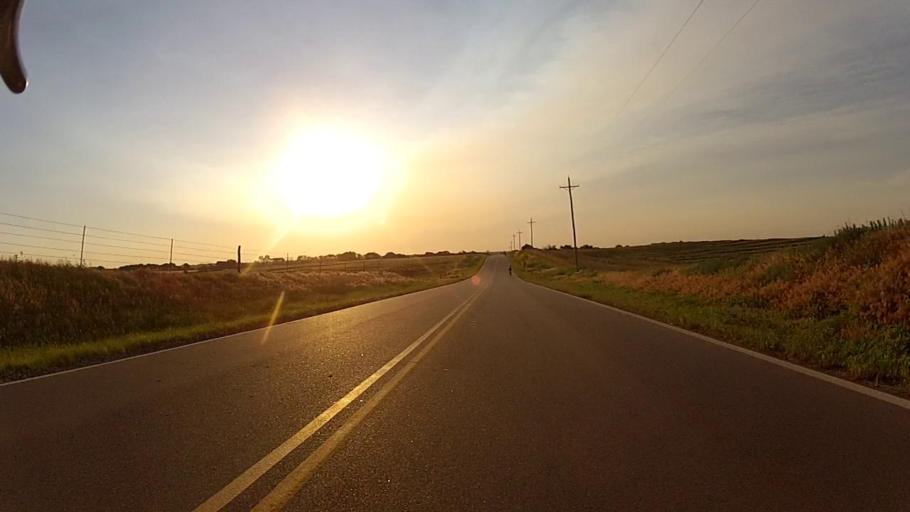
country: US
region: Kansas
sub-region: Harper County
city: Anthony
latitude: 37.1527
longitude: -97.9431
